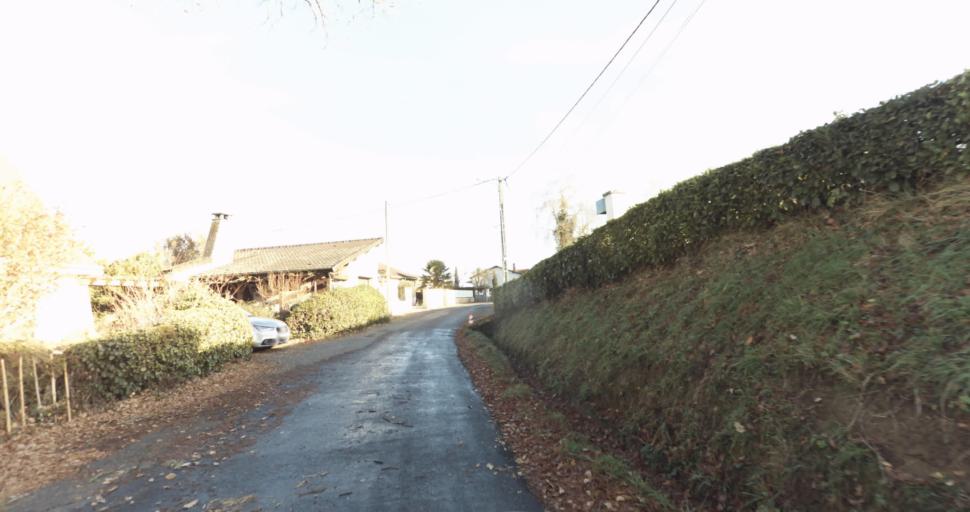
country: FR
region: Limousin
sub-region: Departement de la Haute-Vienne
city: Aixe-sur-Vienne
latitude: 45.7962
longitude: 1.1193
